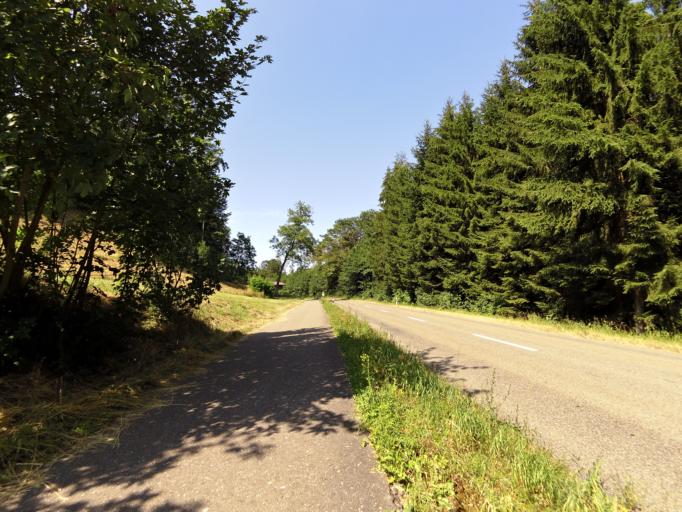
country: CH
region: Aargau
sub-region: Bezirk Brugg
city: Windisch
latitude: 47.4664
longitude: 8.2299
